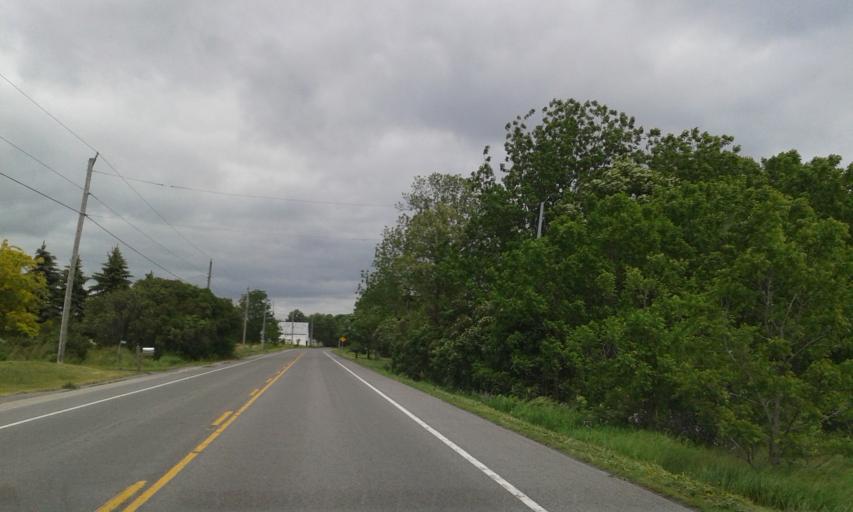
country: CA
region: Ontario
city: Napanee Downtown
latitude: 44.1070
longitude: -76.9268
